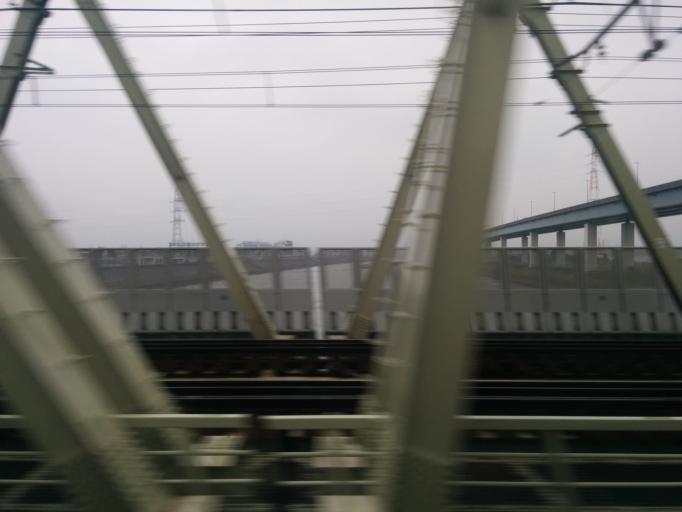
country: JP
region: Tokyo
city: Urayasu
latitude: 35.7133
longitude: 139.8525
